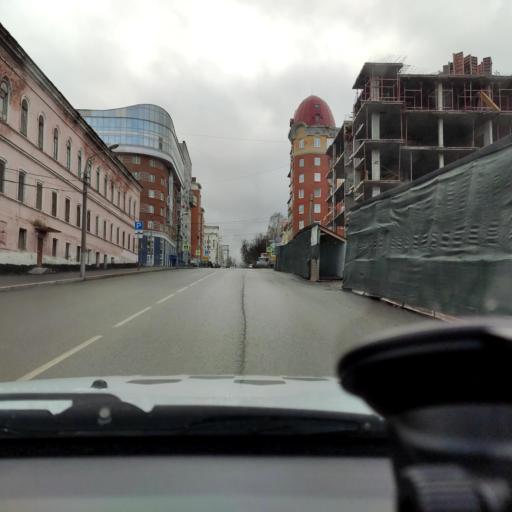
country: RU
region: Perm
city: Perm
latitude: 58.0182
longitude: 56.2537
